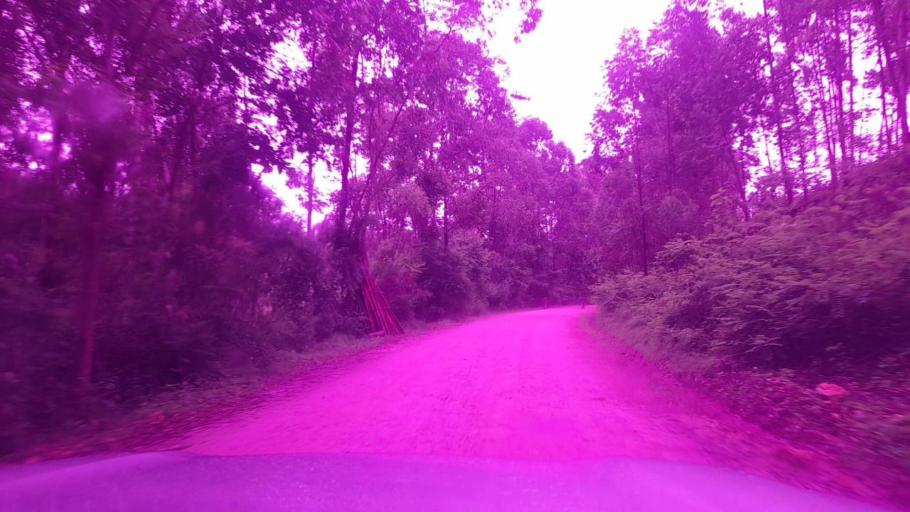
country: ET
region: Southern Nations, Nationalities, and People's Region
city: Bonga
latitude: 7.4571
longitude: 36.1262
